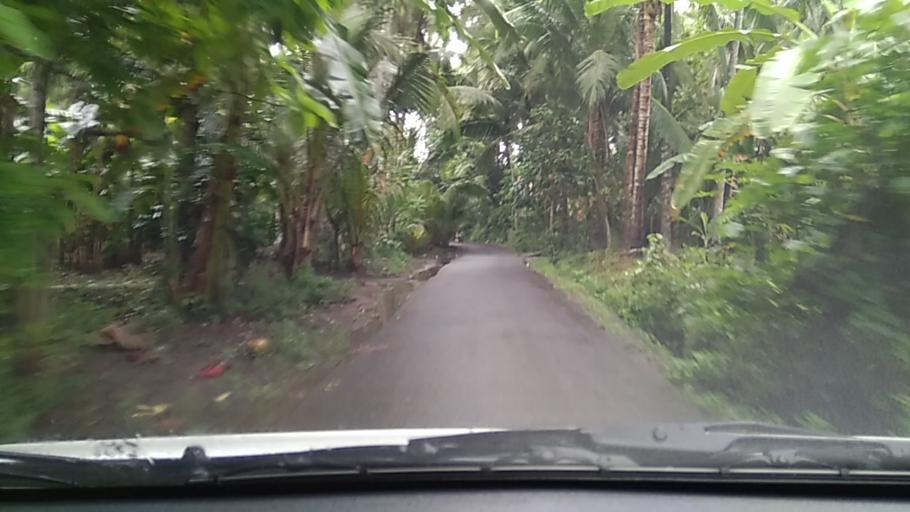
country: ID
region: Bali
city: Banjar Bugbug
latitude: -8.5096
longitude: 115.5788
